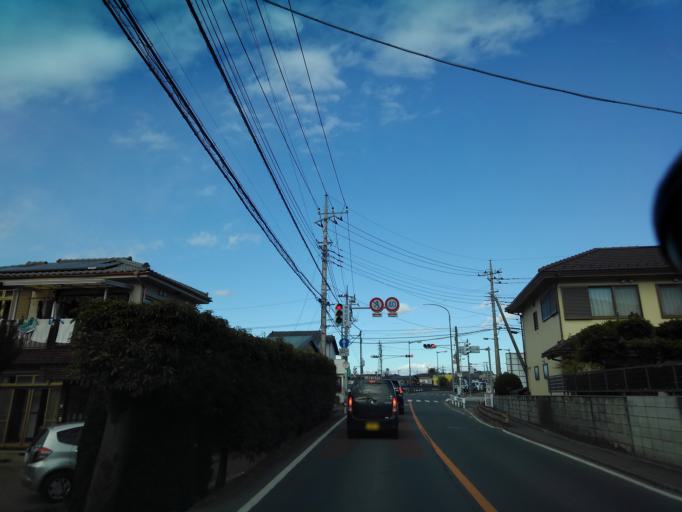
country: JP
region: Saitama
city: Hanno
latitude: 35.8362
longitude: 139.3262
